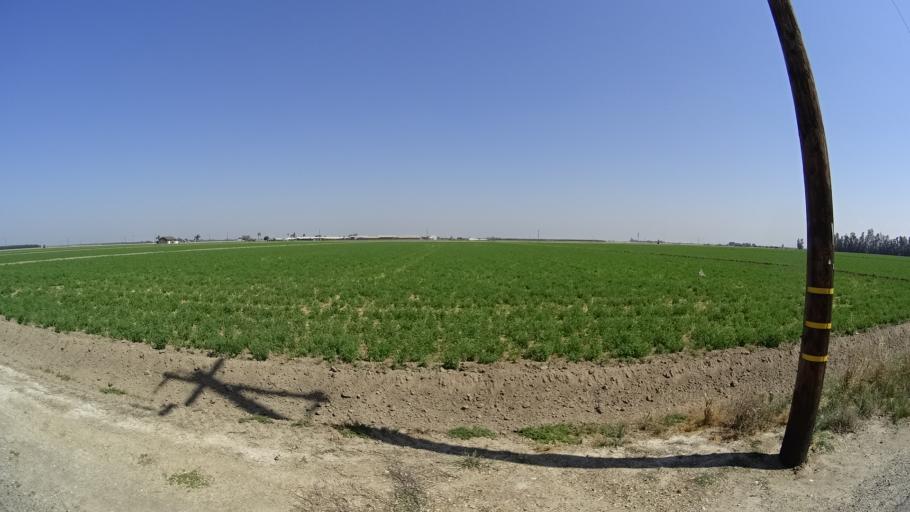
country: US
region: California
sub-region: Kings County
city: Hanford
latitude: 36.3721
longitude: -119.5427
